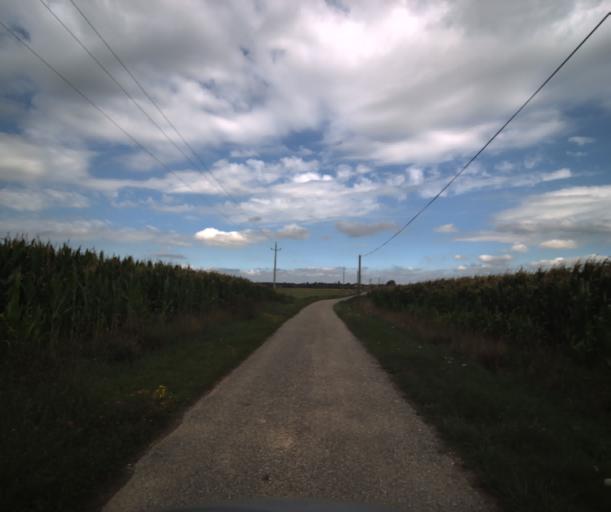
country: FR
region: Midi-Pyrenees
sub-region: Departement de la Haute-Garonne
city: Lacasse
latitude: 43.3949
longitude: 1.2396
